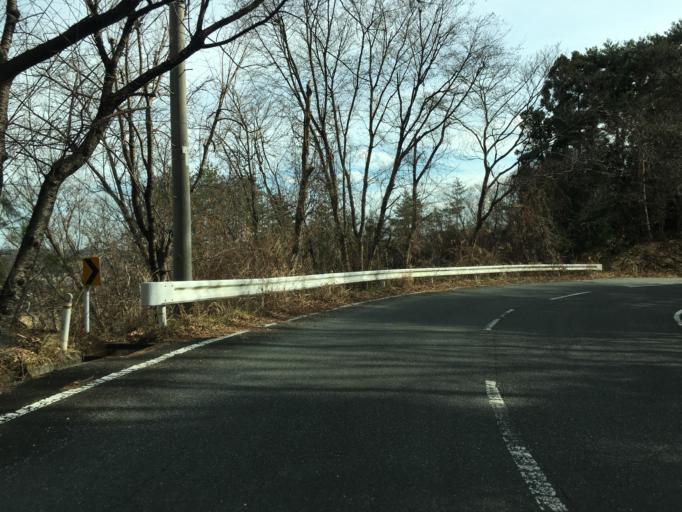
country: JP
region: Fukushima
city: Iwaki
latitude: 37.1281
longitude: 140.8293
